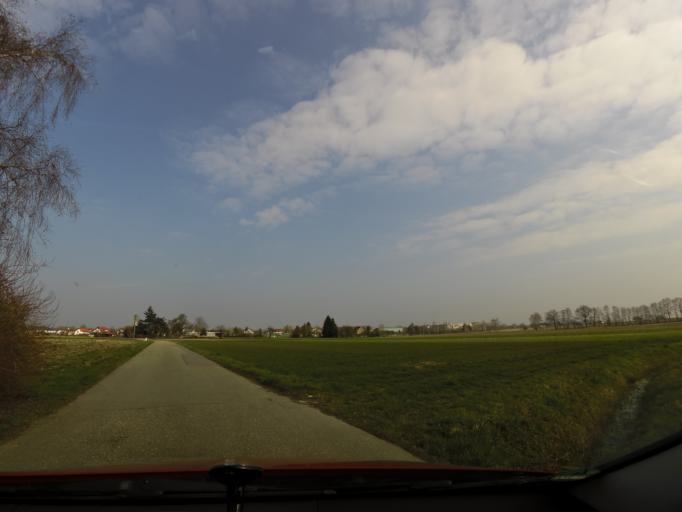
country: DE
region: Baden-Wuerttemberg
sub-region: Freiburg Region
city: Kehl
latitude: 48.5919
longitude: 7.8677
